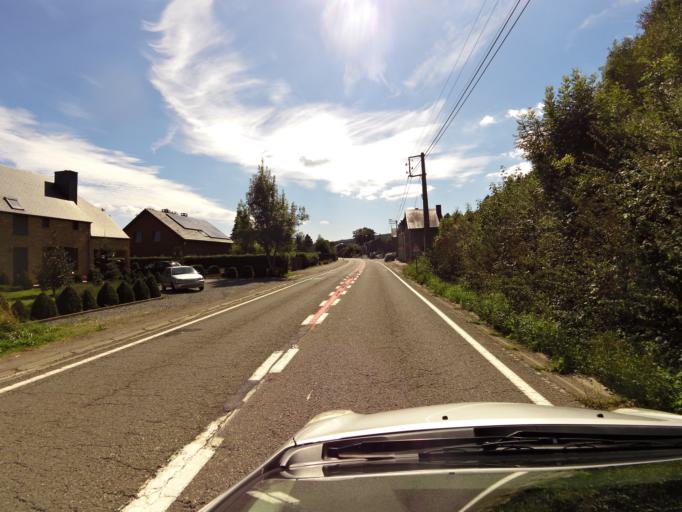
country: BE
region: Wallonia
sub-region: Province du Luxembourg
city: Rendeux
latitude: 50.2449
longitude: 5.4966
